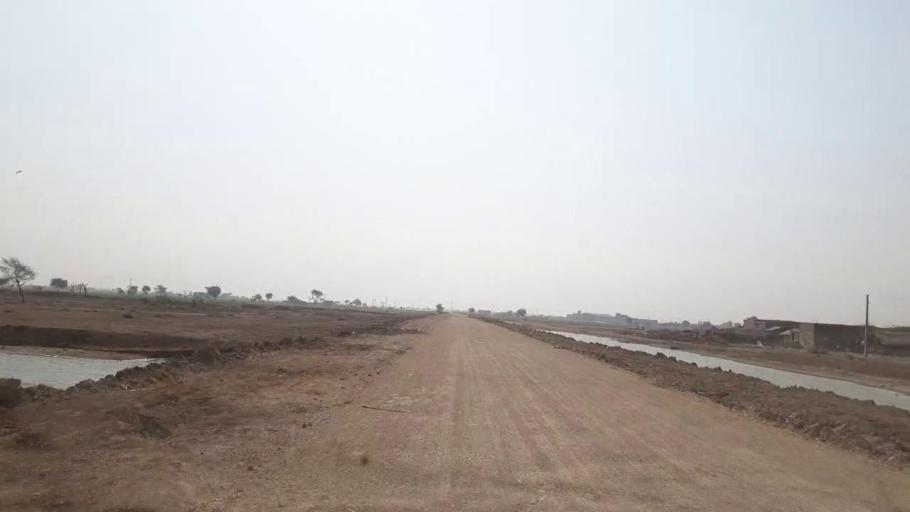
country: PK
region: Sindh
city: Mirpur Khas
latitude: 25.5574
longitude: 69.0473
